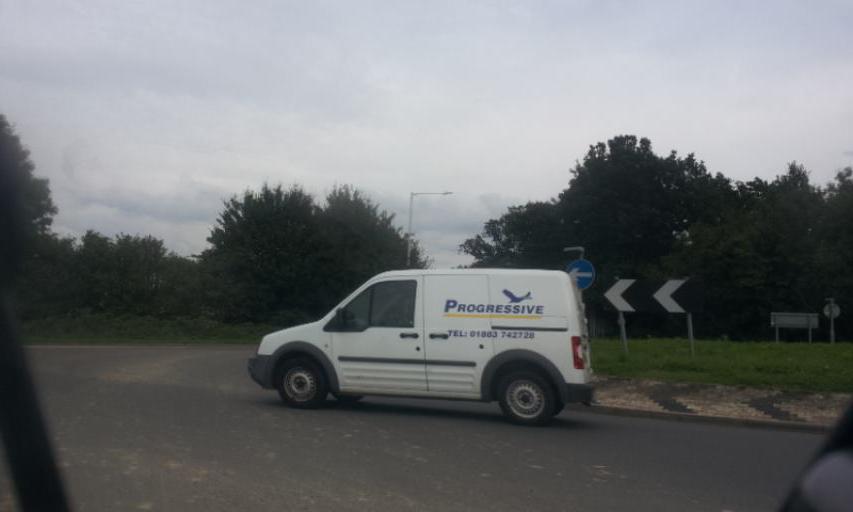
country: GB
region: England
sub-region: Kent
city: Tonbridge
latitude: 51.1857
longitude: 0.2935
